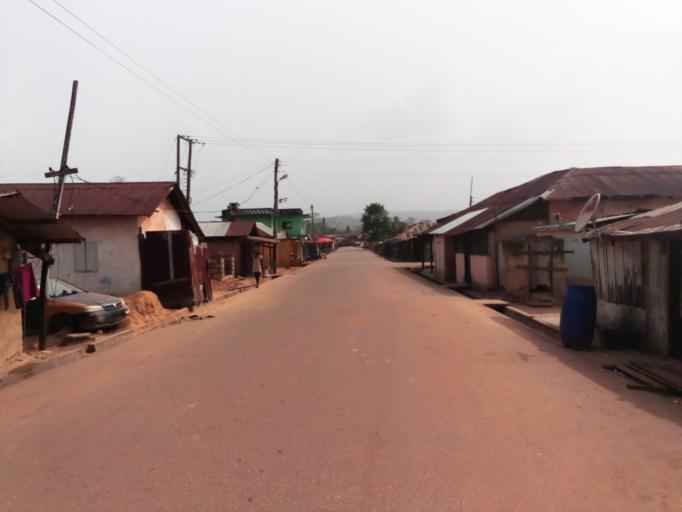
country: CI
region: Sud-Comoe
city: Ayame
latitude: 5.8235
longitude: -2.8195
